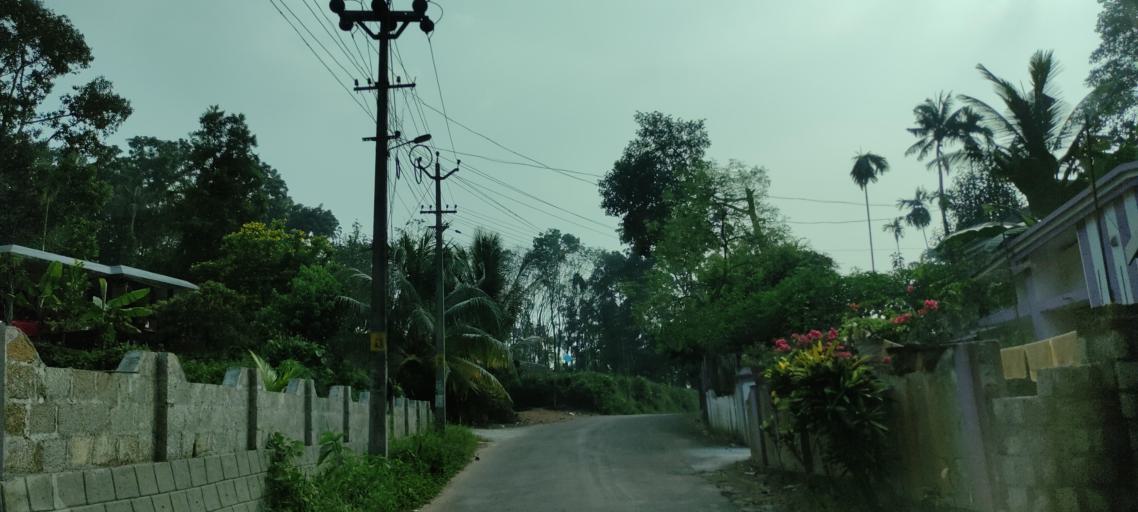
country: IN
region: Kerala
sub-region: Ernakulam
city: Piravam
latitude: 9.7985
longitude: 76.5353
